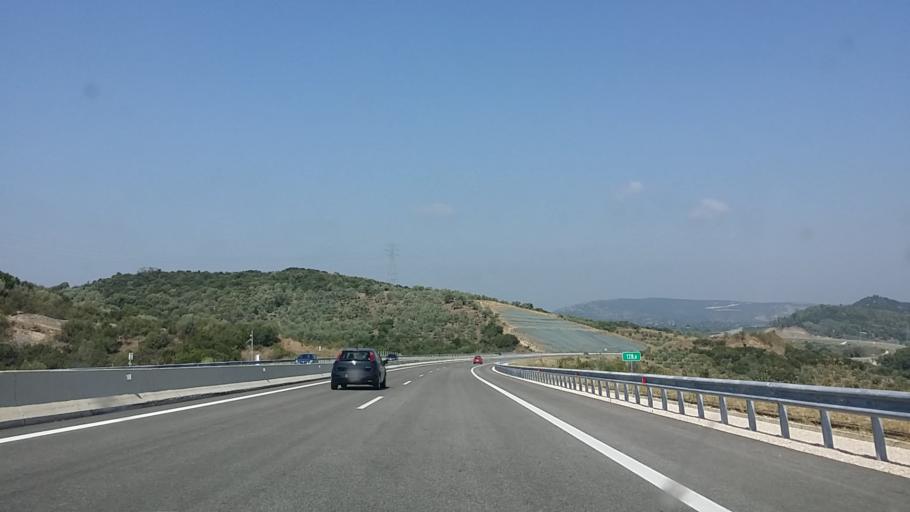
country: GR
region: Epirus
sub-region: Nomos Artas
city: Kompoti
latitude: 39.0756
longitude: 21.1046
